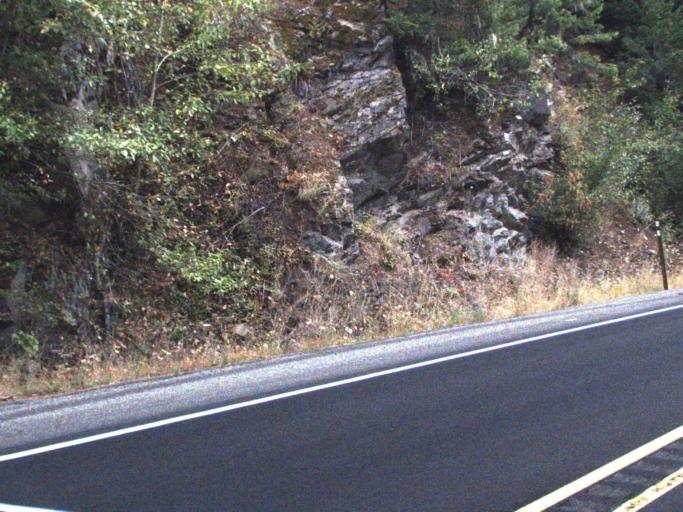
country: US
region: Washington
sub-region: Pierce County
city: Buckley
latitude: 46.6779
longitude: -121.5276
